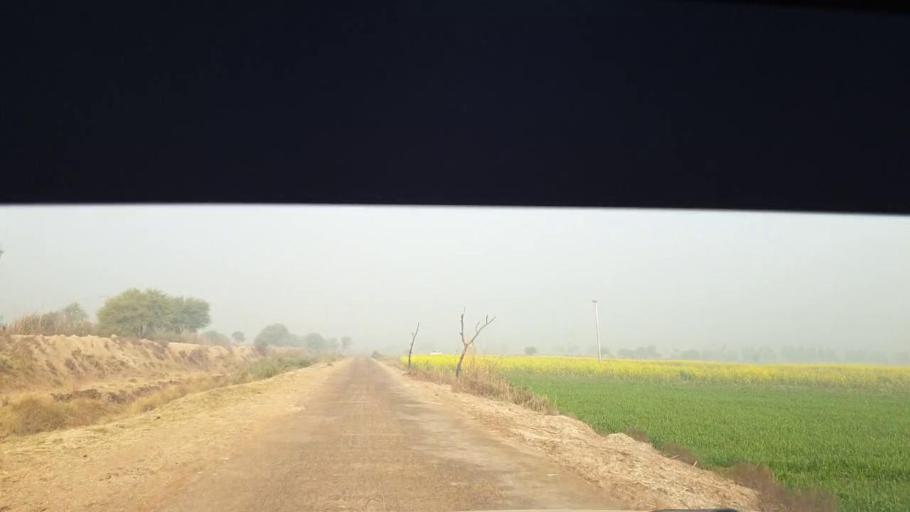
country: PK
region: Sindh
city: Berani
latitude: 25.7832
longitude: 68.7726
